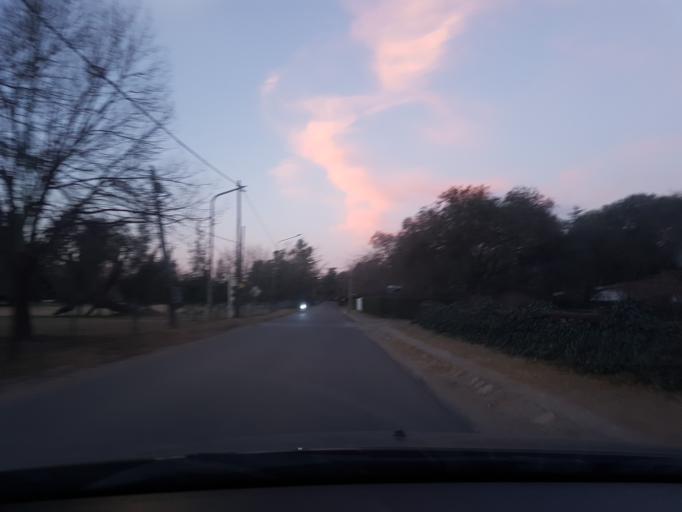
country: AR
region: Cordoba
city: Villa Allende
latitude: -31.2818
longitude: -64.2871
